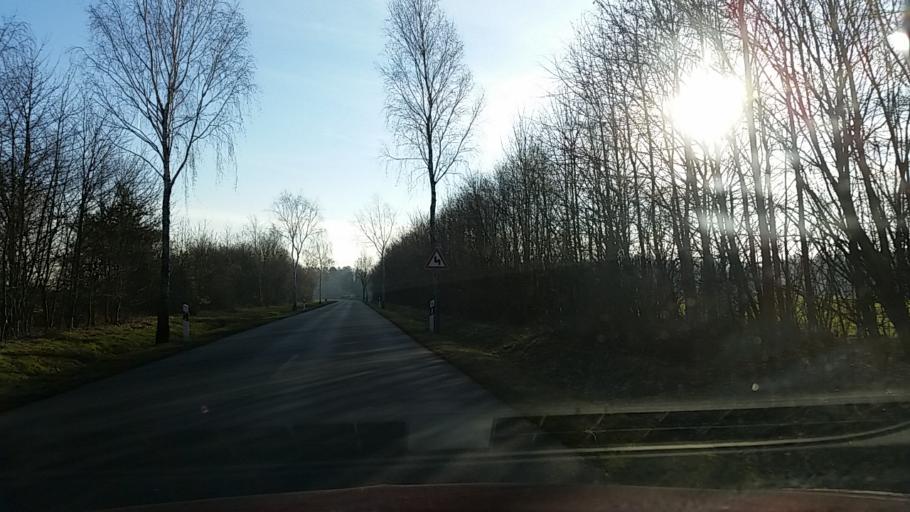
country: DE
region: Lower Saxony
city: Jembke
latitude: 52.5014
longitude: 10.7505
